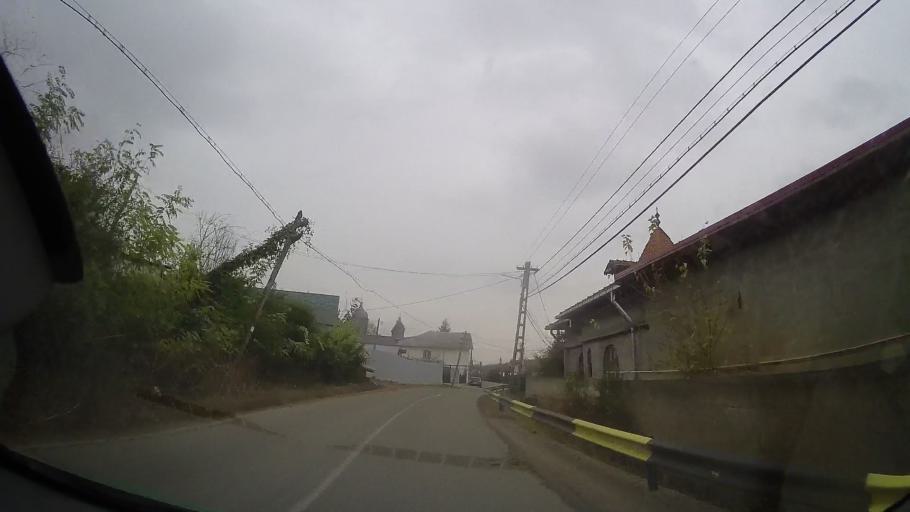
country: RO
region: Prahova
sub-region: Comuna Ceptura
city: Ceptura de Jos
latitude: 45.0288
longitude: 26.3218
